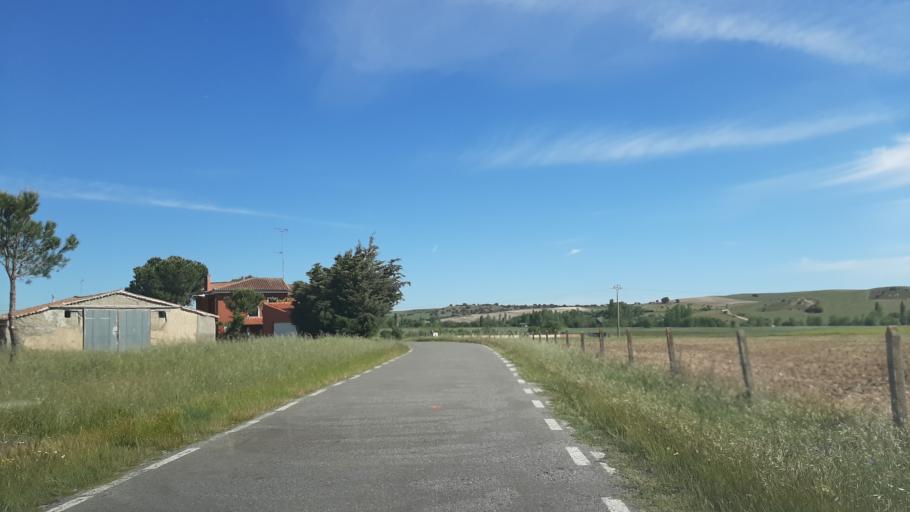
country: ES
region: Castille and Leon
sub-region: Provincia de Salamanca
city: Pedrosillo de Alba
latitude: 40.8077
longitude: -5.3805
